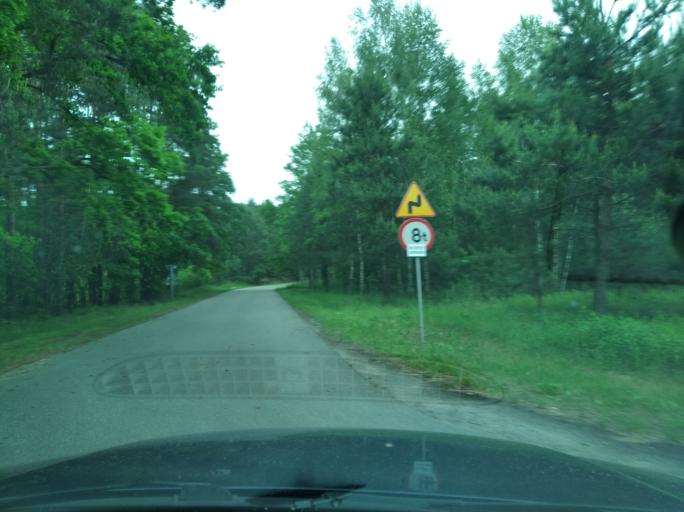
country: PL
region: Subcarpathian Voivodeship
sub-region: Powiat kolbuszowski
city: Niwiska
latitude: 50.2121
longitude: 21.6643
